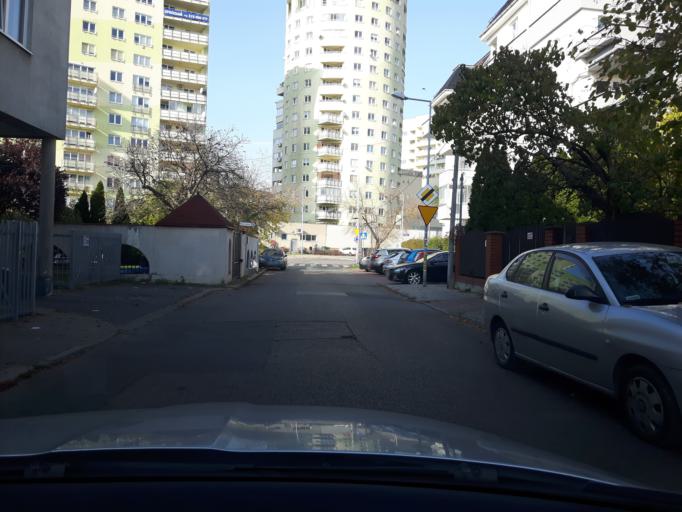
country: PL
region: Masovian Voivodeship
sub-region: Warszawa
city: Praga Poludnie
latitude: 52.2318
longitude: 21.0836
